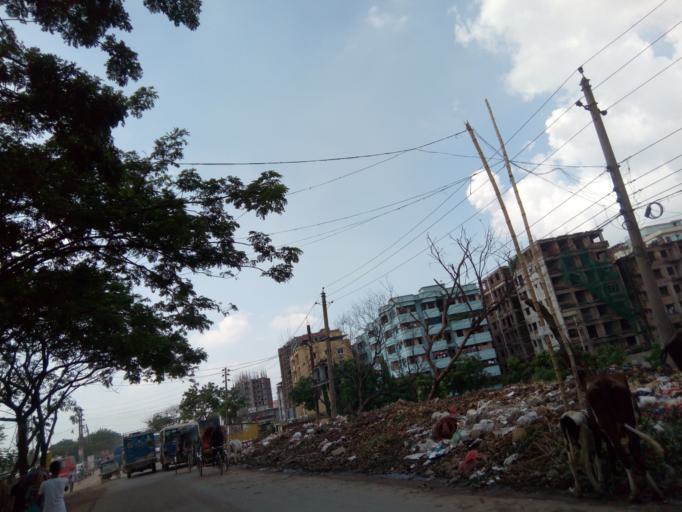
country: BD
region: Dhaka
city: Azimpur
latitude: 23.7426
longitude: 90.3601
